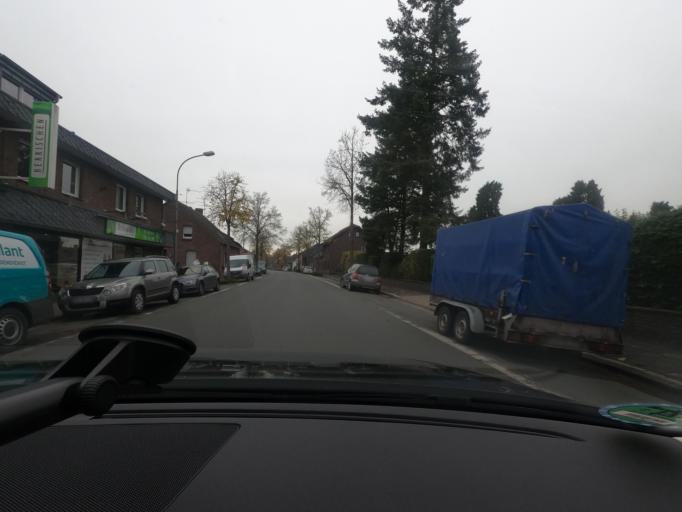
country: DE
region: North Rhine-Westphalia
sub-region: Regierungsbezirk Dusseldorf
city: Wachtendonk
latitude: 51.4595
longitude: 6.3700
